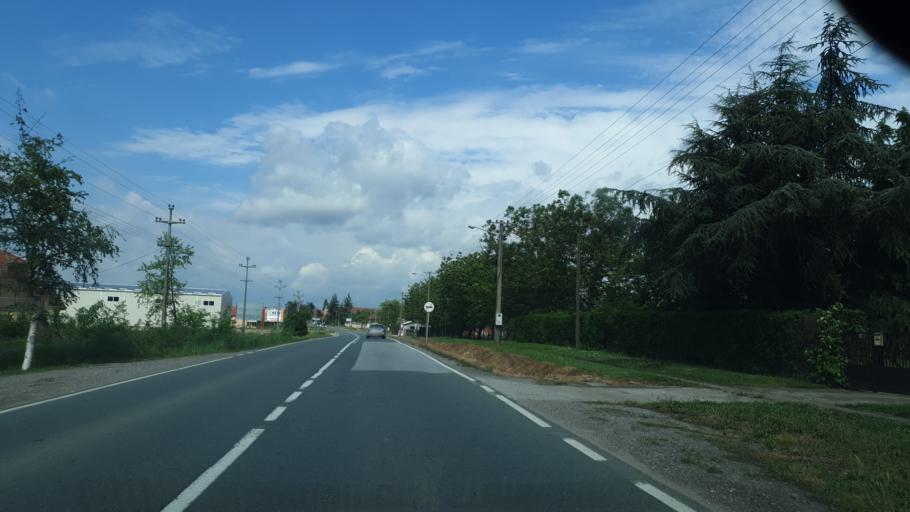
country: RS
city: Zvecka
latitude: 44.6166
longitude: 20.1667
